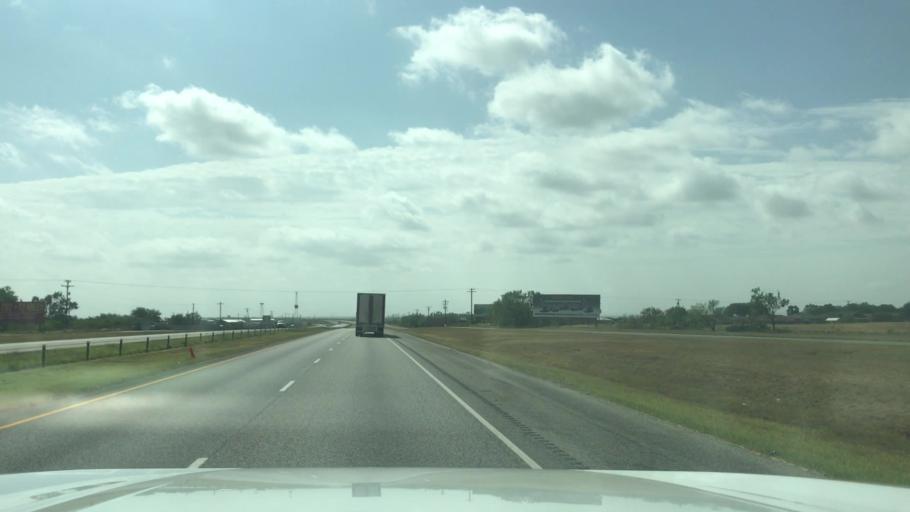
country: US
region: Texas
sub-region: Taylor County
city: Merkel
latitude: 32.4746
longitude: -99.9987
